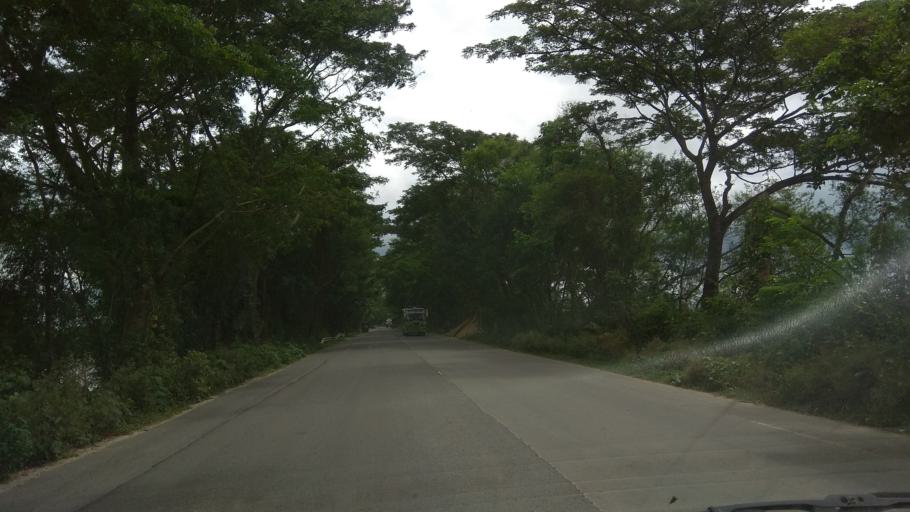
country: BD
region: Khulna
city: Kalia
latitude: 23.2296
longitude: 89.7379
